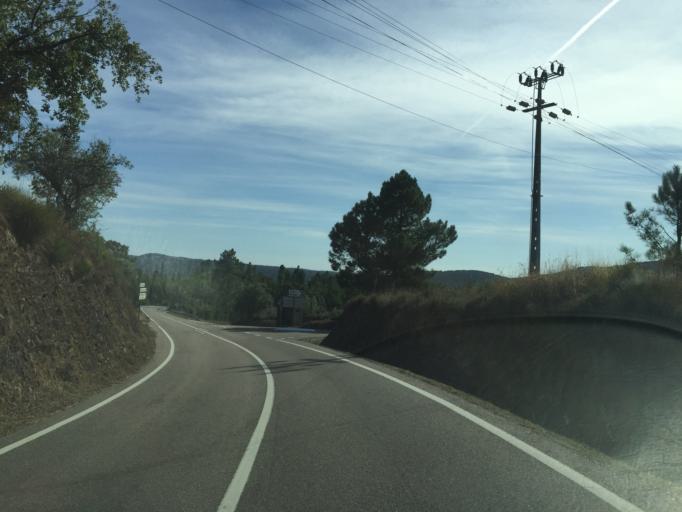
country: PT
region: Portalegre
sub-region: Marvao
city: Marvao
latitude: 39.4001
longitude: -7.3917
